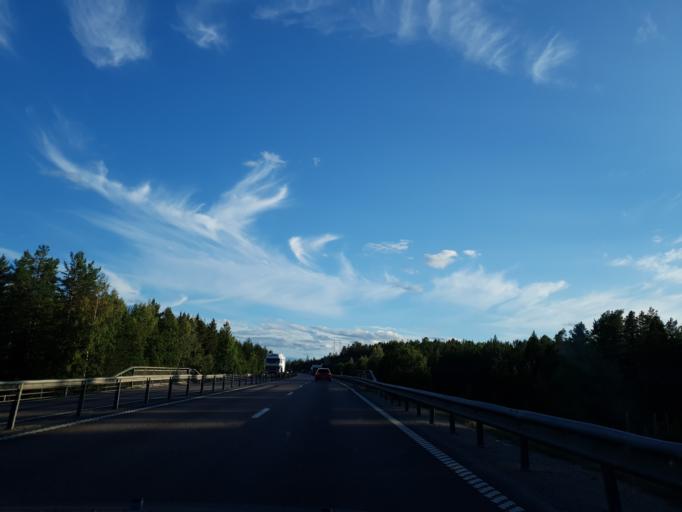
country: SE
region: Gaevleborg
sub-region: Hudiksvalls Kommun
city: Hudiksvall
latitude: 61.7391
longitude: 17.0717
